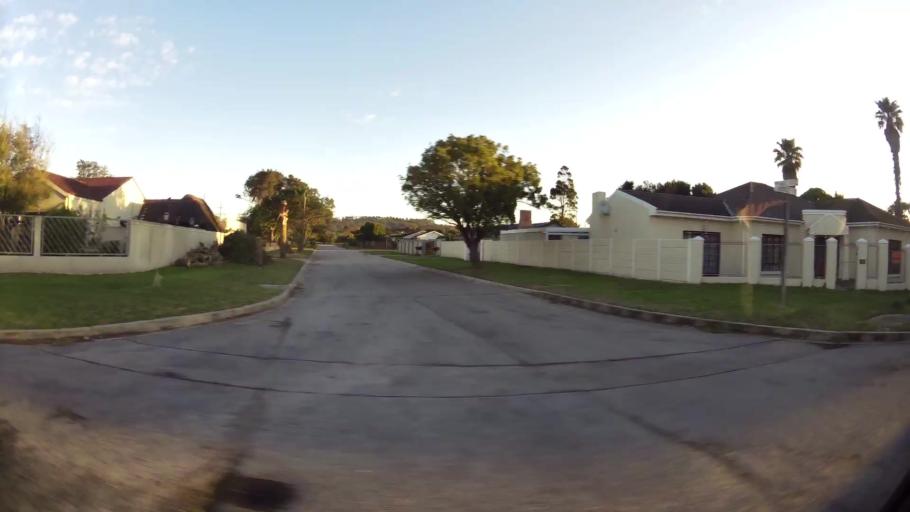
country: ZA
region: Eastern Cape
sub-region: Nelson Mandela Bay Metropolitan Municipality
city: Port Elizabeth
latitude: -33.9741
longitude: 25.5255
